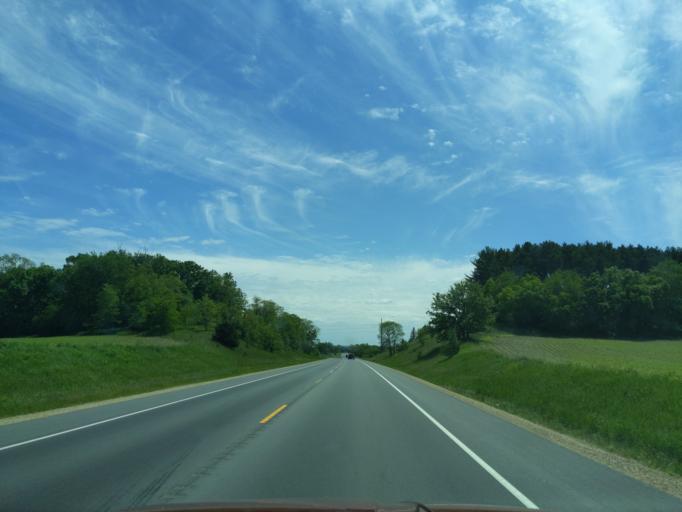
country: US
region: Wisconsin
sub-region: Columbia County
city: Pardeeville
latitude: 43.5659
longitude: -89.3058
